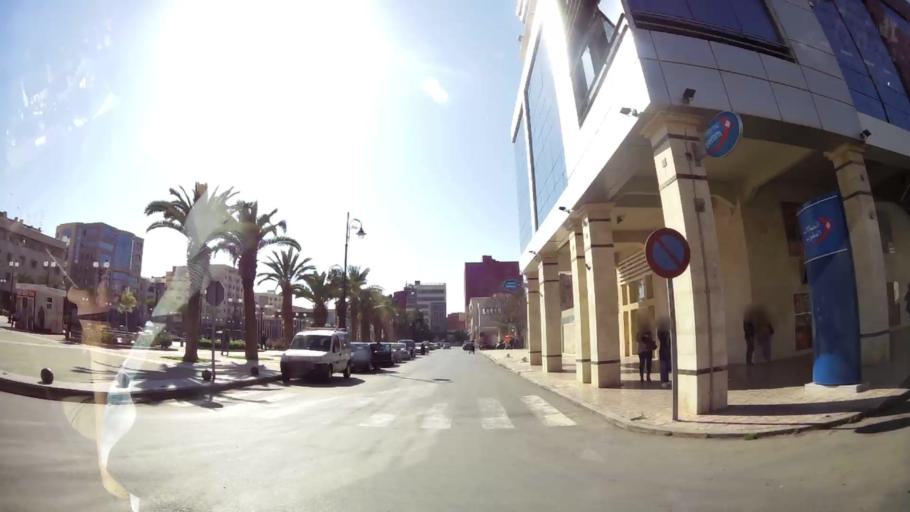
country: MA
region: Oriental
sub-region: Oujda-Angad
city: Oujda
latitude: 34.6848
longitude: -1.9150
